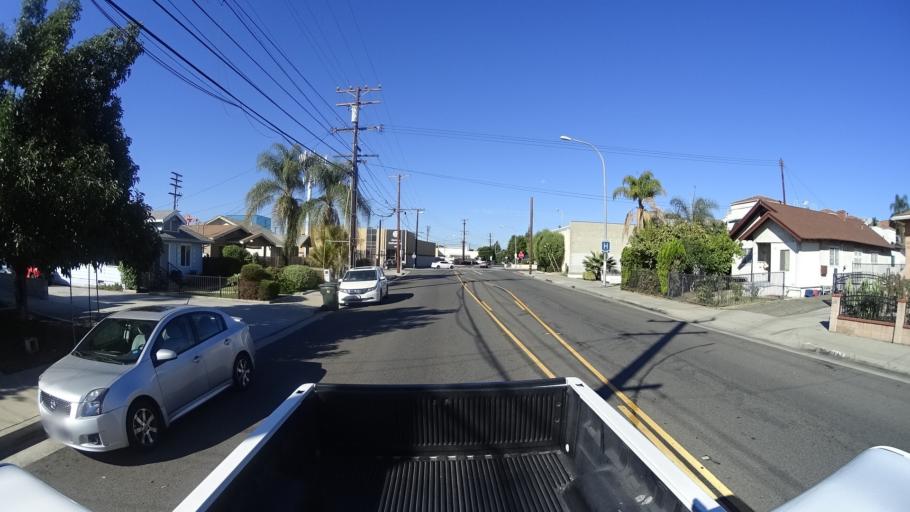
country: US
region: California
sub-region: Los Angeles County
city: Alhambra
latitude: 34.0875
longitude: -118.1440
